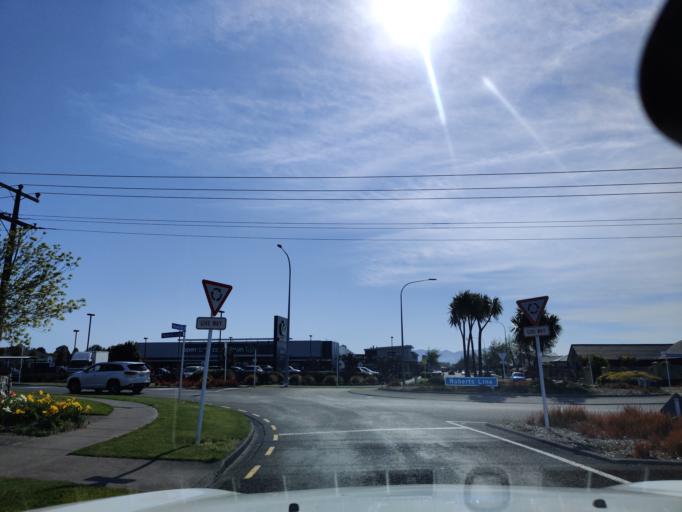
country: NZ
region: Manawatu-Wanganui
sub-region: Palmerston North City
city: Palmerston North
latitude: -40.3307
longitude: 175.6520
